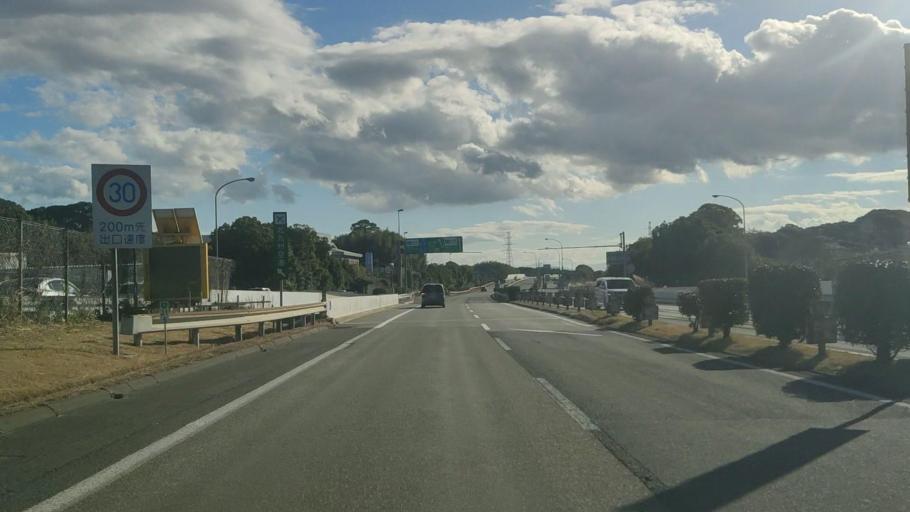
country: JP
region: Fukuoka
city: Nakama
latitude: 33.7890
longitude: 130.7458
